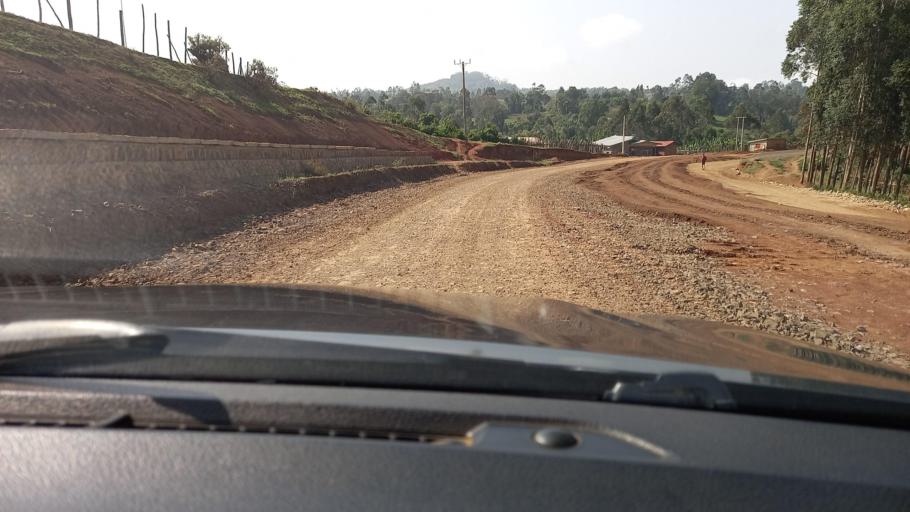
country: ET
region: Southern Nations, Nationalities, and People's Region
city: Mizan Teferi
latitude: 6.1732
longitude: 35.5862
